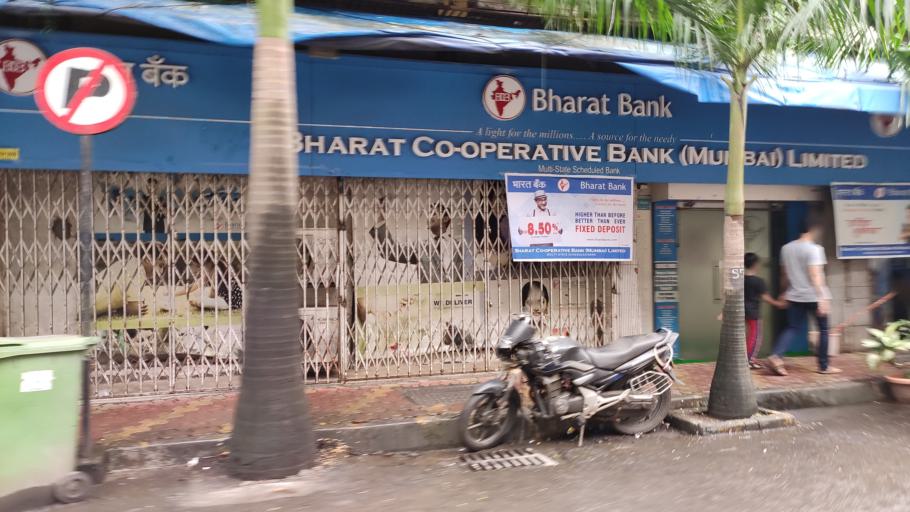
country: IN
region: Maharashtra
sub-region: Mumbai Suburban
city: Borivli
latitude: 19.2129
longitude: 72.8675
